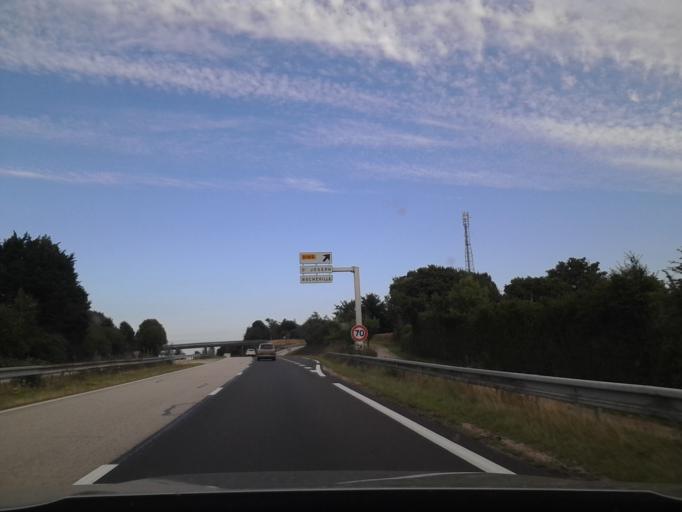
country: FR
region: Lower Normandy
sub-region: Departement de la Manche
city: Brix
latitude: 49.5352
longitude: -1.5347
